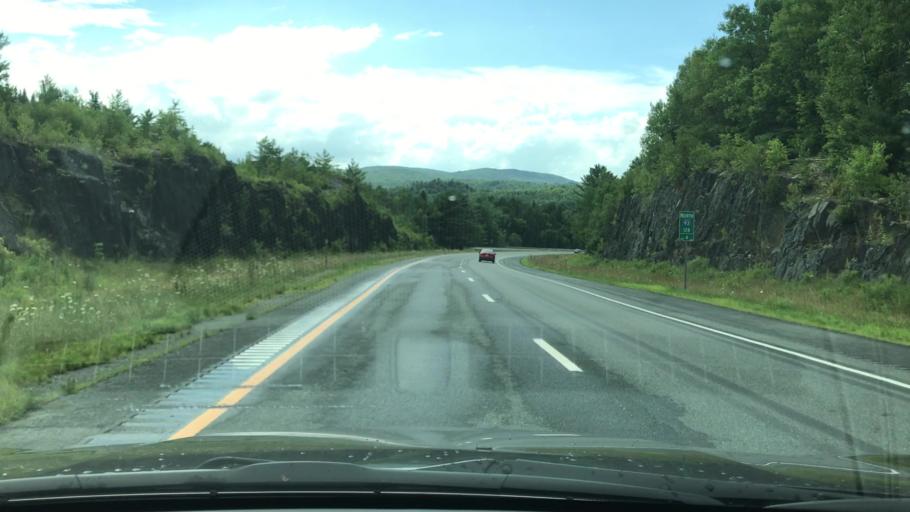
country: US
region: New Hampshire
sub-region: Grafton County
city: Littleton
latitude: 44.3134
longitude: -71.8492
